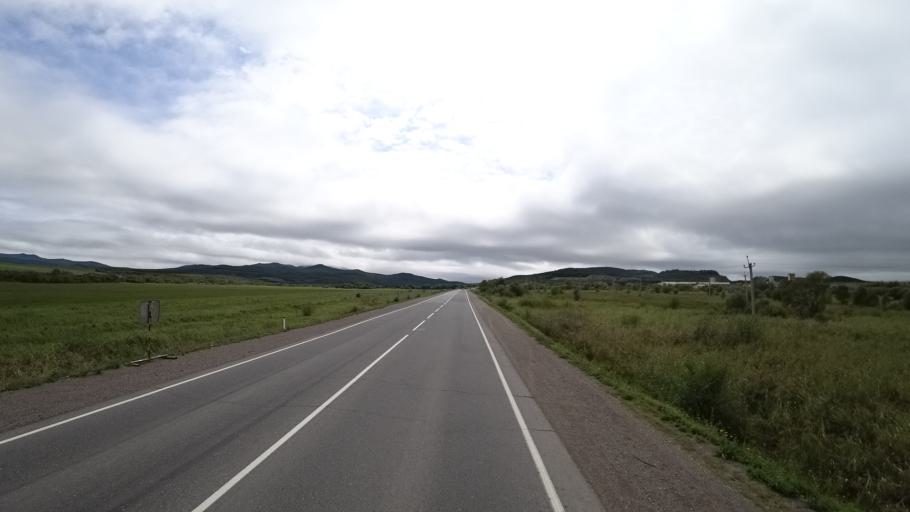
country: RU
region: Primorskiy
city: Monastyrishche
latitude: 44.1755
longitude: 132.4413
